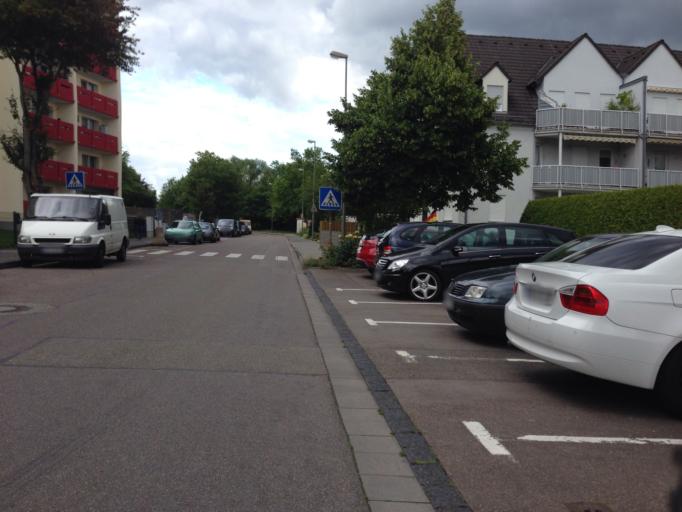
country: DE
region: Hesse
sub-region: Regierungsbezirk Darmstadt
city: Hanau am Main
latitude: 50.1315
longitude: 8.8869
